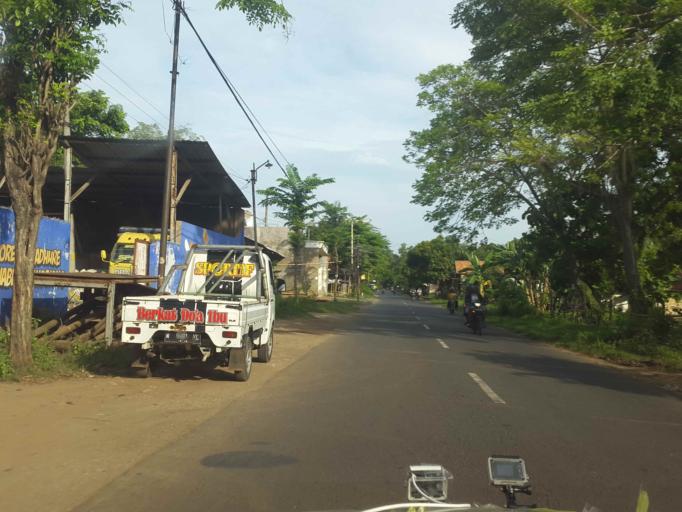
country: ID
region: East Java
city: Bereklorong
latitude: -7.0387
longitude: 113.9135
